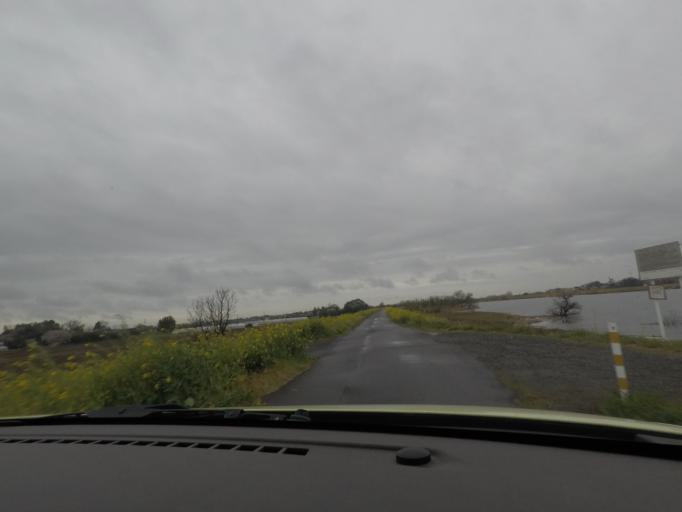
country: JP
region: Ibaraki
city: Mitsukaido
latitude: 36.0554
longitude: 140.0182
